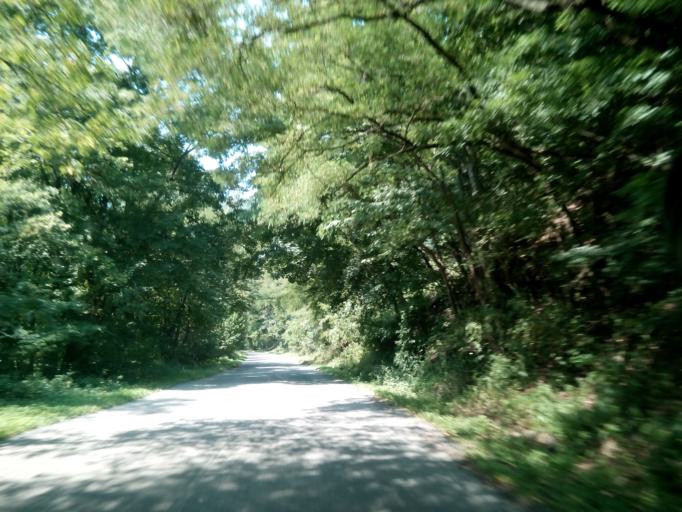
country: SK
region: Presovsky
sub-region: Okres Presov
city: Presov
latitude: 48.8811
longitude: 21.1230
